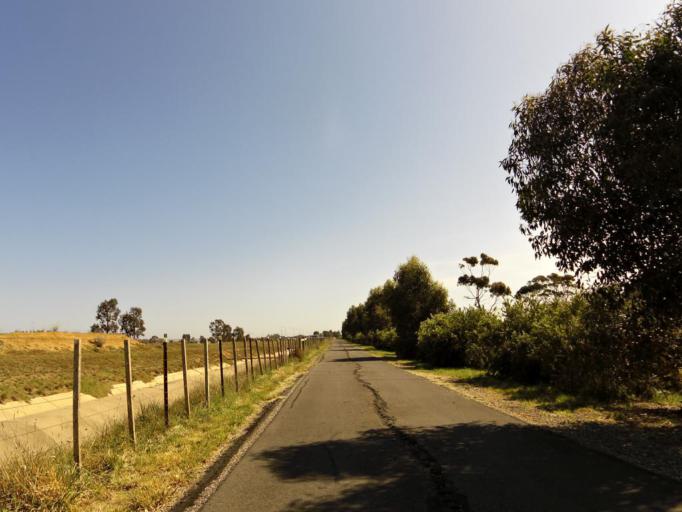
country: AU
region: Victoria
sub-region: Wyndham
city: Werribee
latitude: -37.9078
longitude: 144.6914
